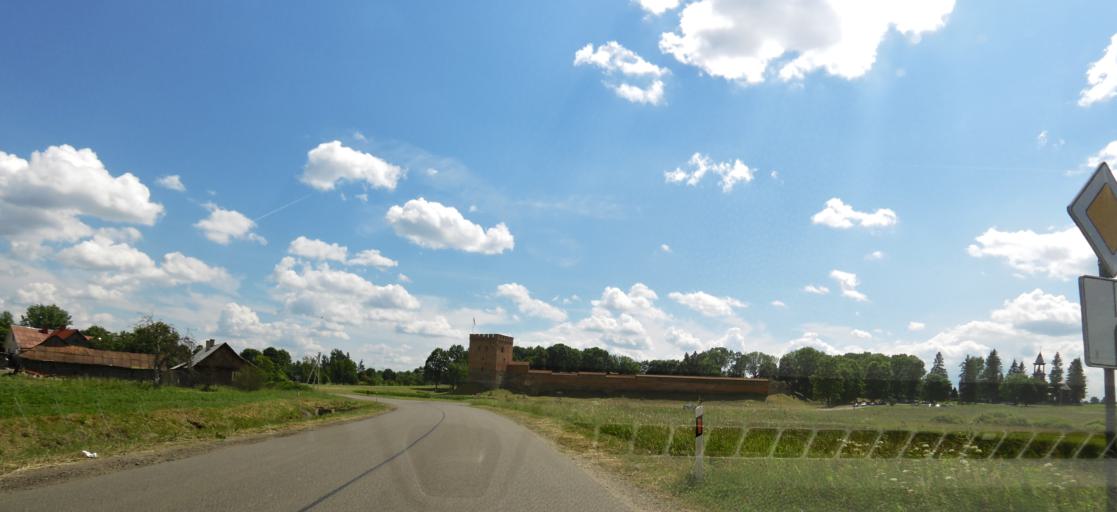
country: LT
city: Skaidiskes
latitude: 54.5423
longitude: 25.6493
